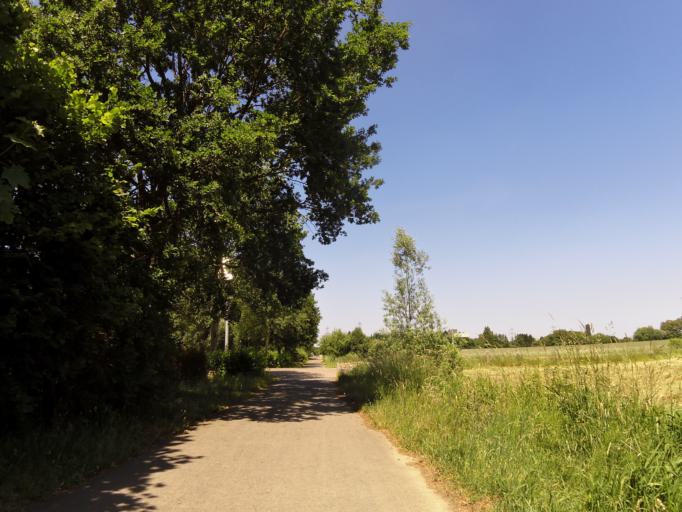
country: DE
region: Hesse
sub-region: Regierungsbezirk Darmstadt
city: Erzhausen
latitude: 49.9661
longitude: 8.6416
